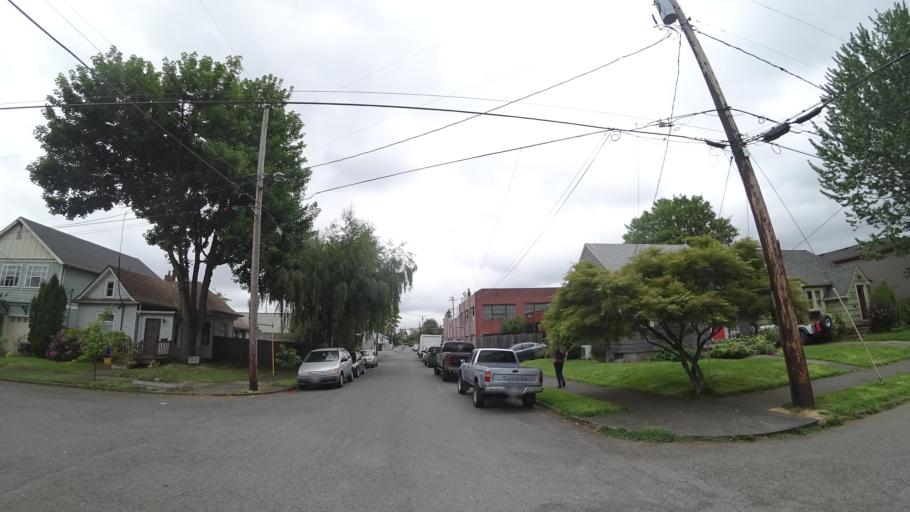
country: US
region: Oregon
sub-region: Multnomah County
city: Lents
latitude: 45.4930
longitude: -122.6054
